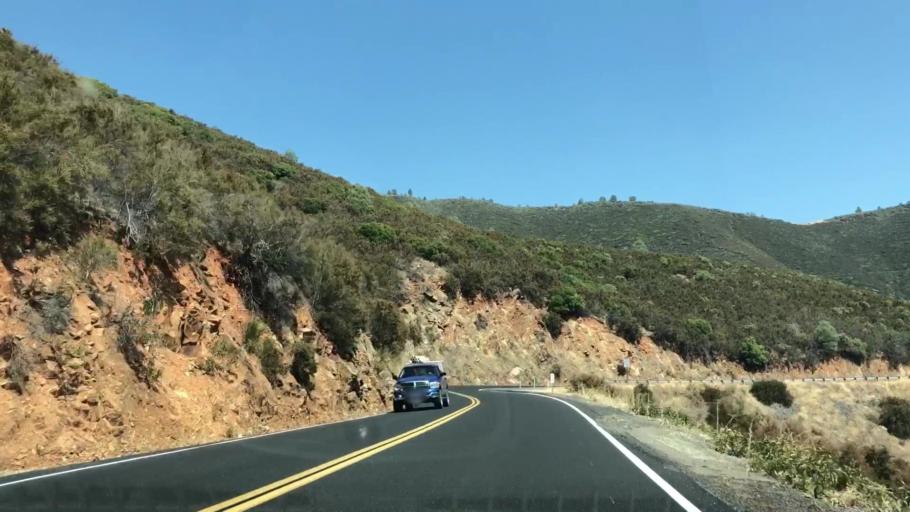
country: US
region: California
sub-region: Tuolumne County
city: Tuolumne City
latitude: 37.8213
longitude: -120.2860
